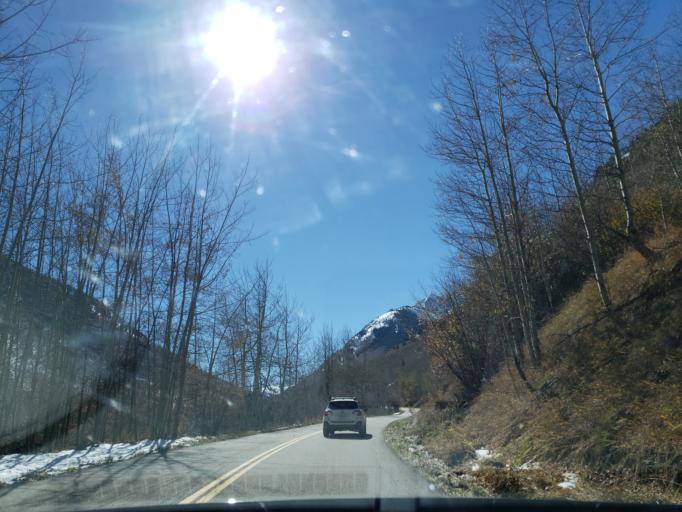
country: US
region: Colorado
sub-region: Pitkin County
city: Snowmass Village
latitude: 39.1206
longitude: -106.9088
